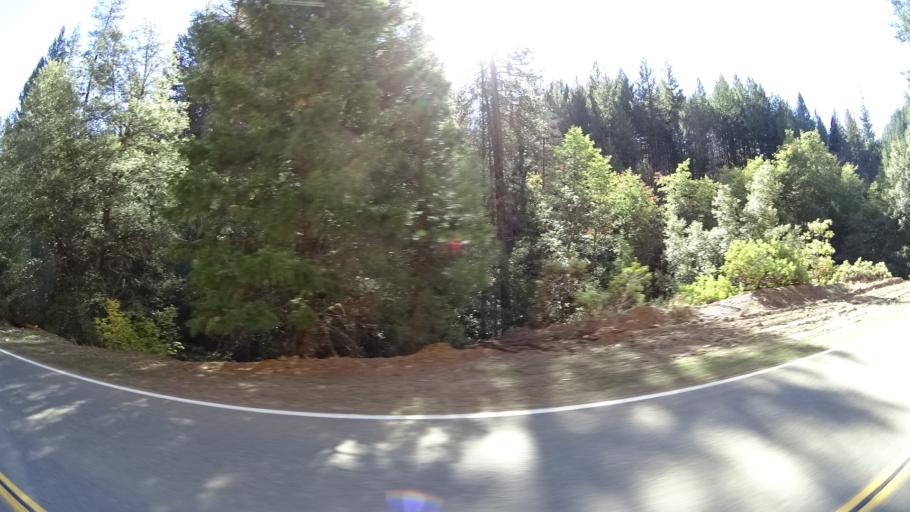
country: US
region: California
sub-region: Trinity County
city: Weaverville
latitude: 41.1722
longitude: -123.0946
